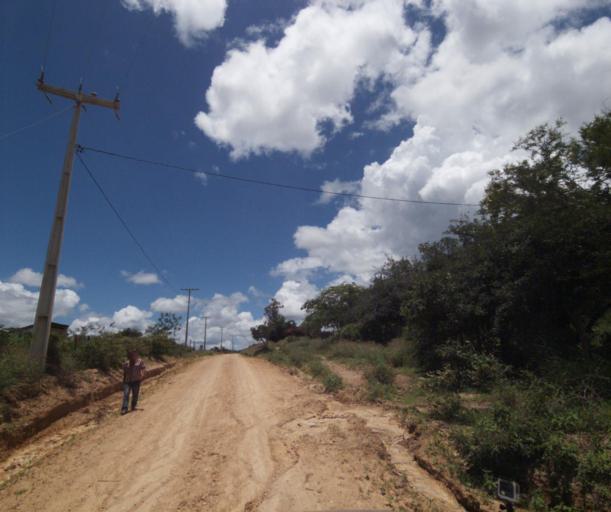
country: BR
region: Bahia
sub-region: Pocoes
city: Pocoes
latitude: -14.3827
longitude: -40.3814
